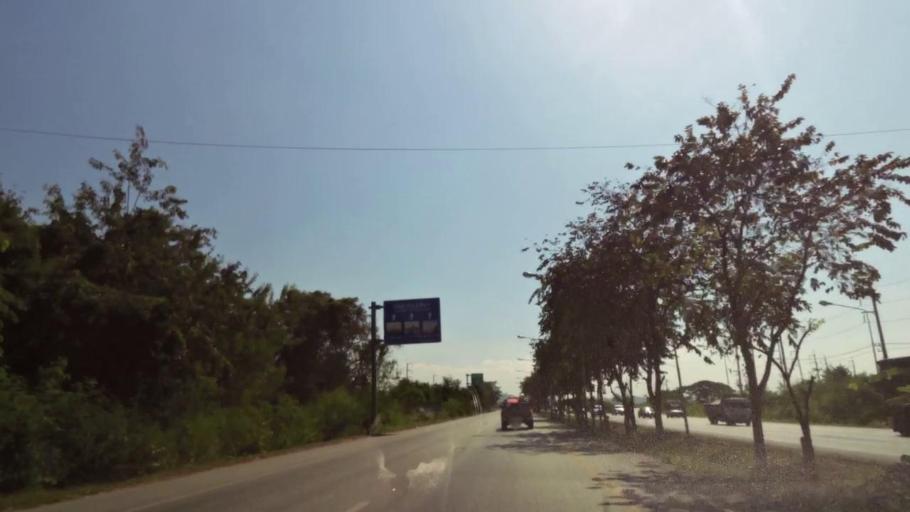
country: TH
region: Nakhon Sawan
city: Nakhon Sawan
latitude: 15.7713
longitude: 100.1213
